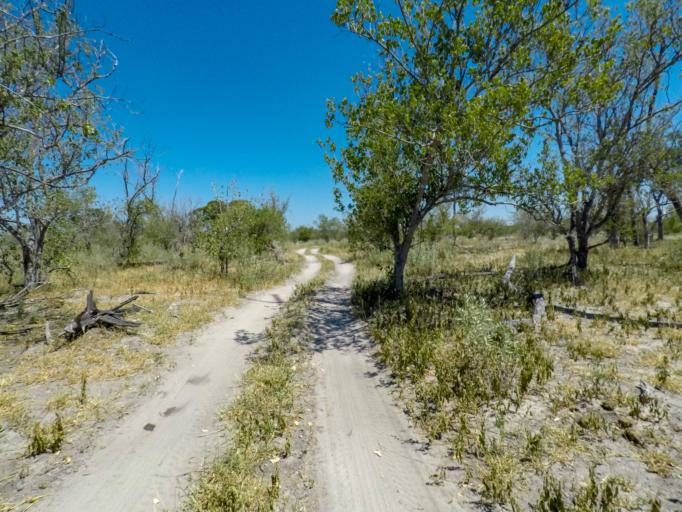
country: BW
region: North West
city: Maun
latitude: -19.4398
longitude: 23.5611
